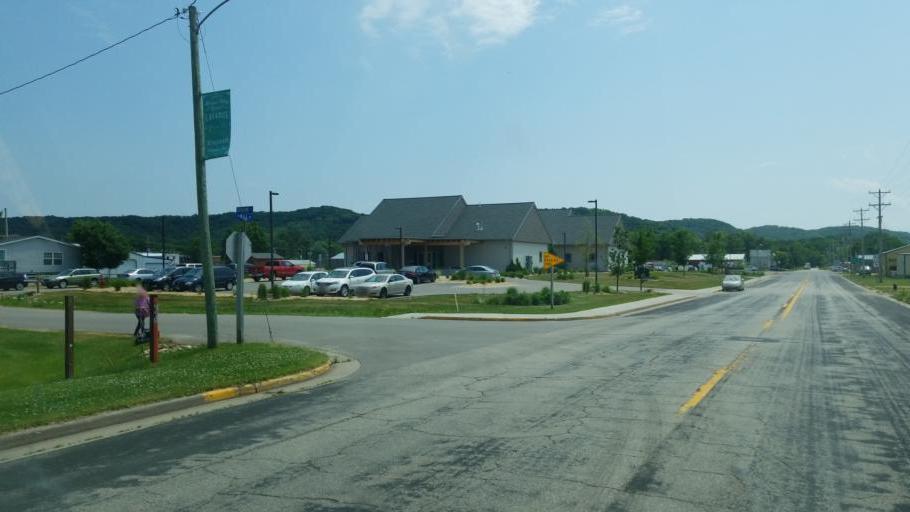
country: US
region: Wisconsin
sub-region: Monroe County
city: Cashton
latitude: 43.5764
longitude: -90.6414
